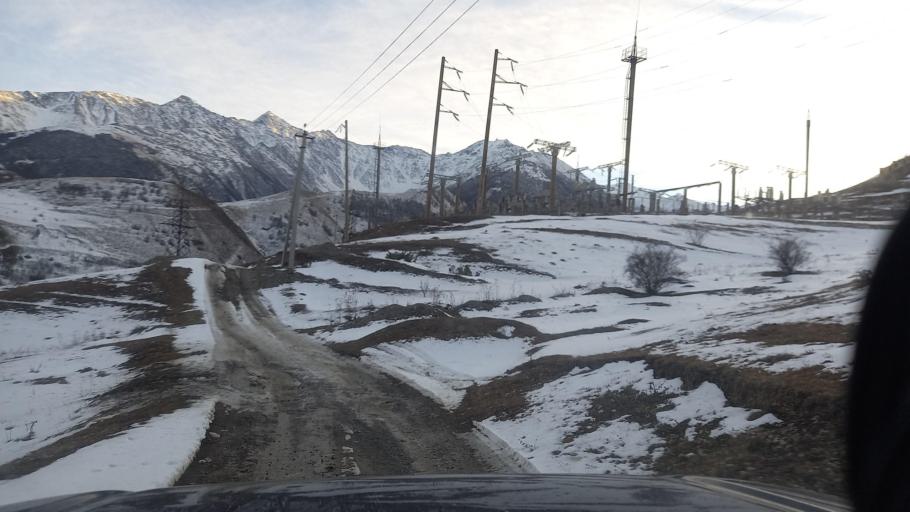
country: RU
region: Ingushetiya
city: Dzhayrakh
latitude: 42.8467
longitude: 44.5131
